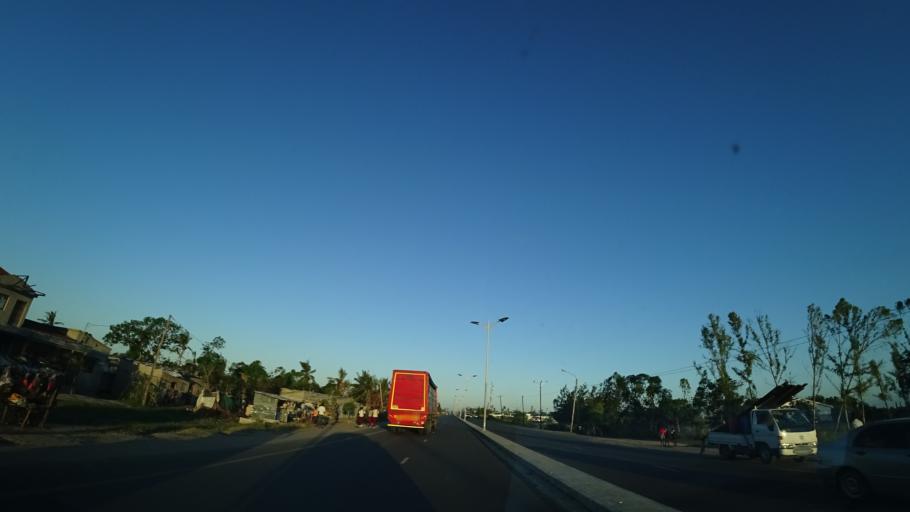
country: MZ
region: Sofala
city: Beira
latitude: -19.7282
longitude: 34.8193
